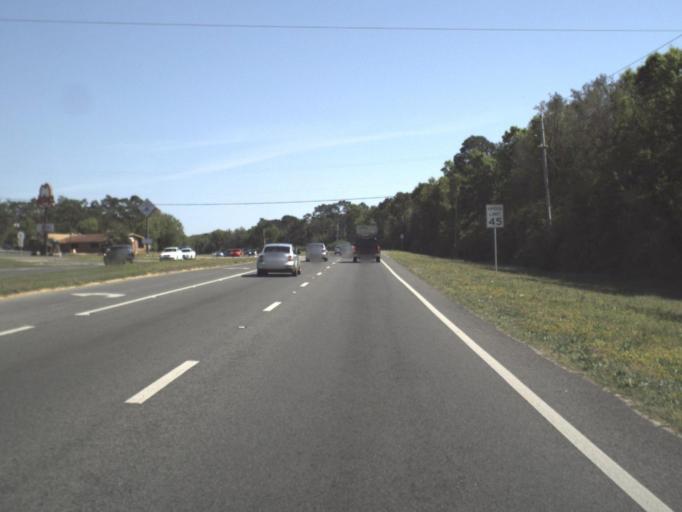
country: US
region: Florida
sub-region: Escambia County
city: Bellview
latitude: 30.4583
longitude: -87.2997
